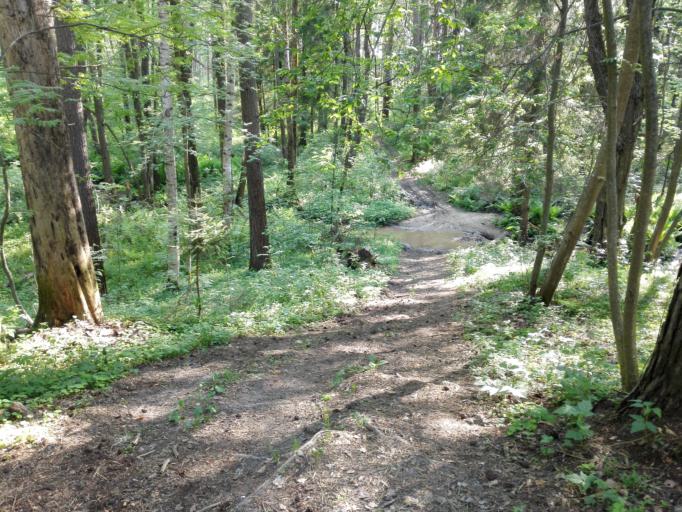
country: RU
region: Vladimir
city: Kommunar
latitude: 56.0609
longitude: 40.5046
